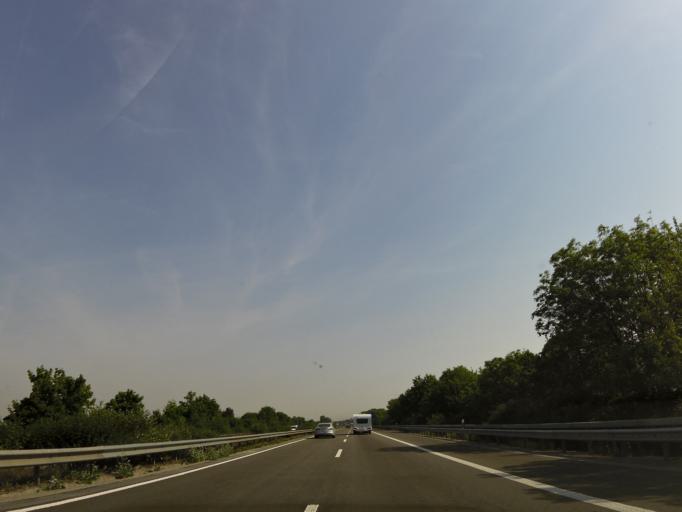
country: DE
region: Rheinland-Pfalz
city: Kleinniedesheim
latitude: 49.6118
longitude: 8.2907
